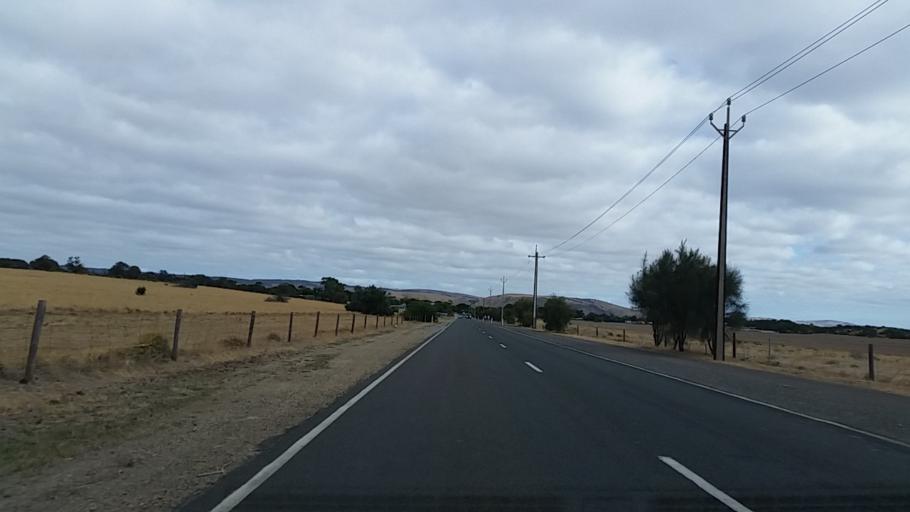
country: AU
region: South Australia
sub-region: Yankalilla
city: Normanville
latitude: -35.4371
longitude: 138.3200
